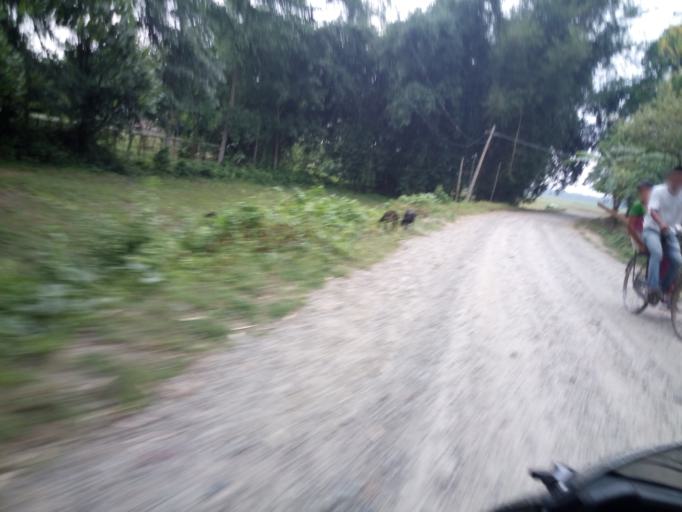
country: IN
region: Assam
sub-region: Darrang
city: Kharupatia
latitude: 26.6513
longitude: 92.2449
